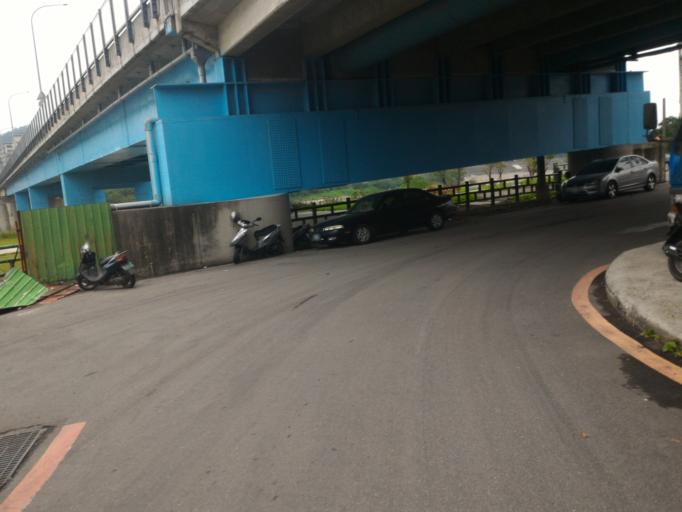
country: TW
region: Taiwan
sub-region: Taoyuan
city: Taoyuan
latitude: 24.9649
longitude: 121.3945
